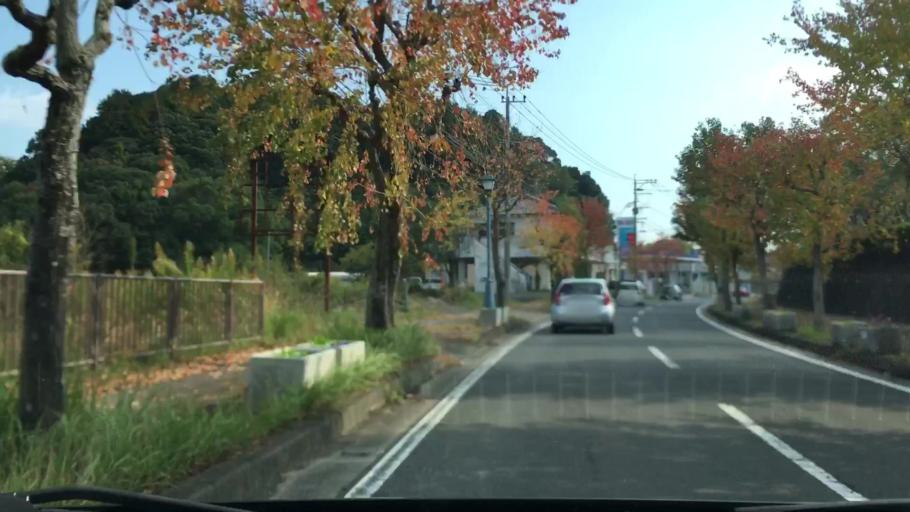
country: JP
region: Nagasaki
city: Sasebo
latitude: 32.9910
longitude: 129.7641
